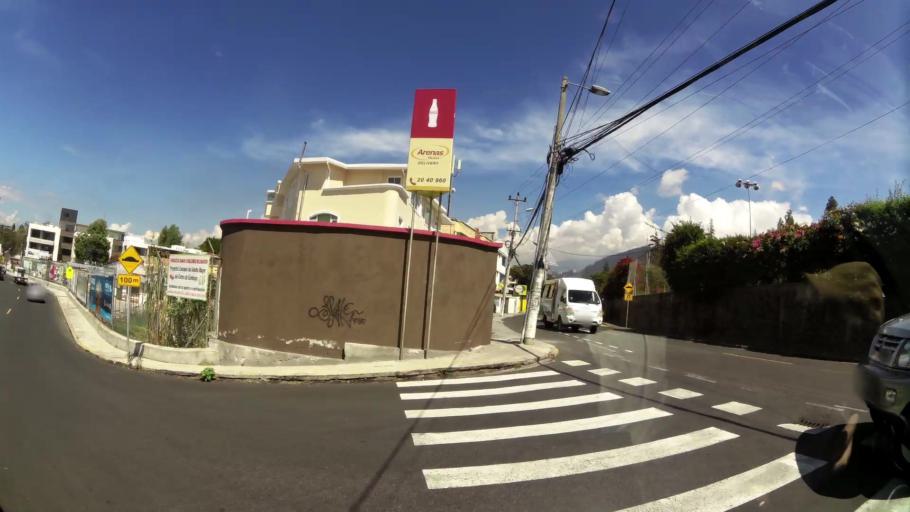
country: EC
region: Pichincha
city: Quito
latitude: -0.1971
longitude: -78.4272
